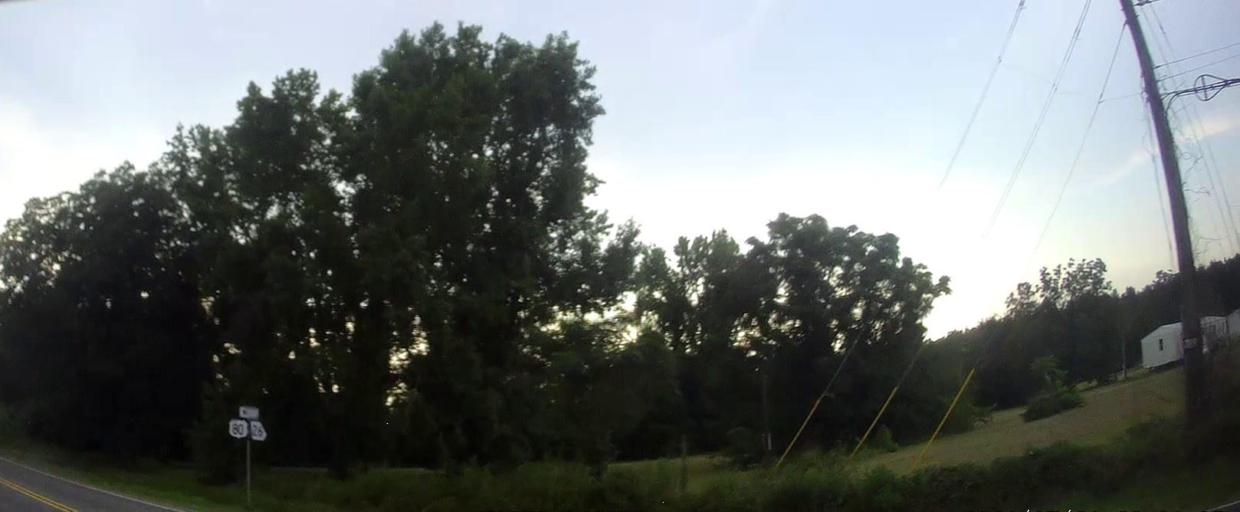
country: US
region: Georgia
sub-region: Laurens County
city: East Dublin
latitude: 32.5544
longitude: -82.8380
